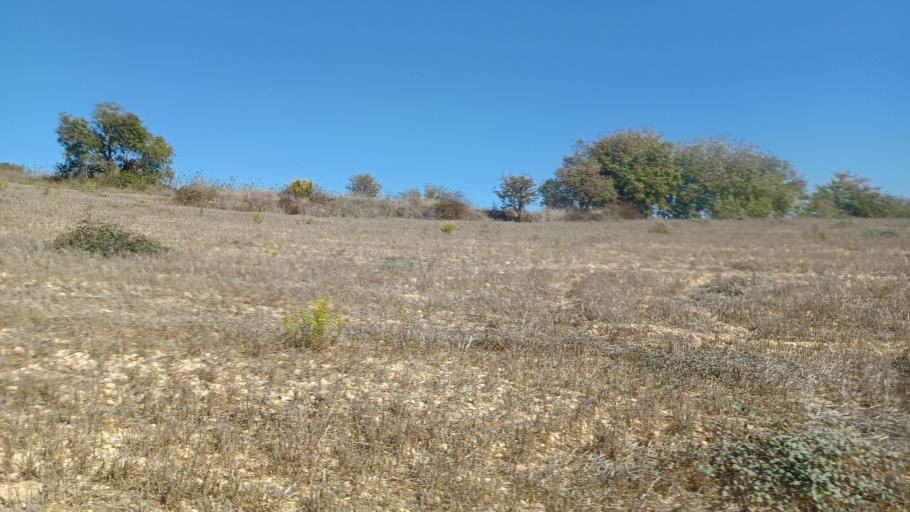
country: CY
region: Pafos
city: Mesogi
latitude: 34.8121
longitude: 32.4869
